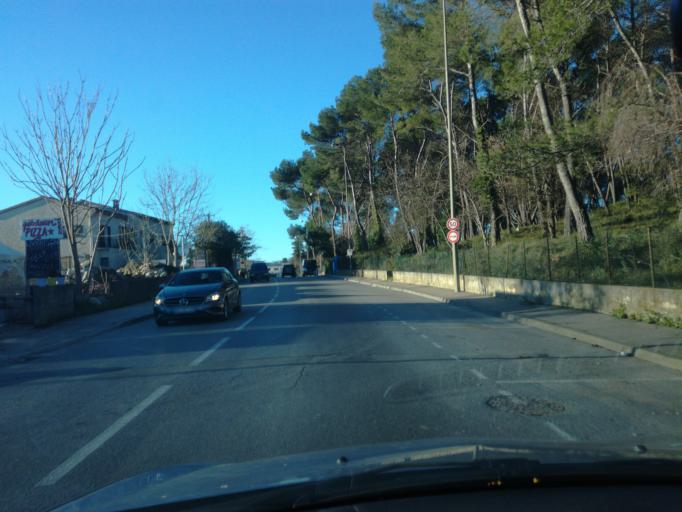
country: FR
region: Provence-Alpes-Cote d'Azur
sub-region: Departement des Alpes-Maritimes
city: La Roquette-sur-Siagne
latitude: 43.6029
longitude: 6.9705
